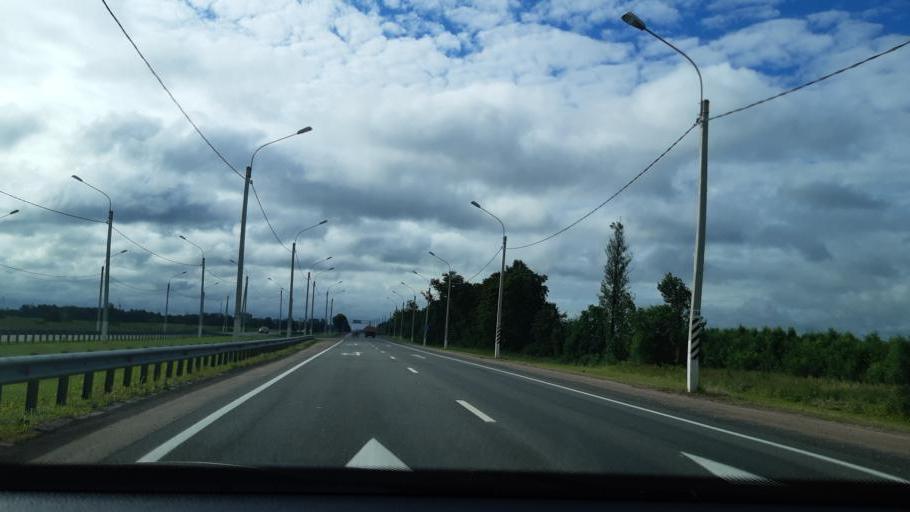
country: RU
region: Smolensk
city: Talashkino
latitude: 54.6989
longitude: 32.1238
